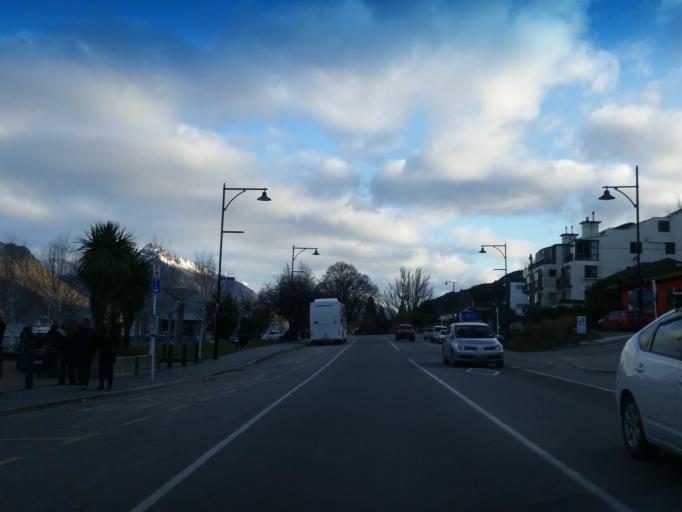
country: NZ
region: Otago
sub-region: Queenstown-Lakes District
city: Queenstown
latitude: -45.0334
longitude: 168.6570
